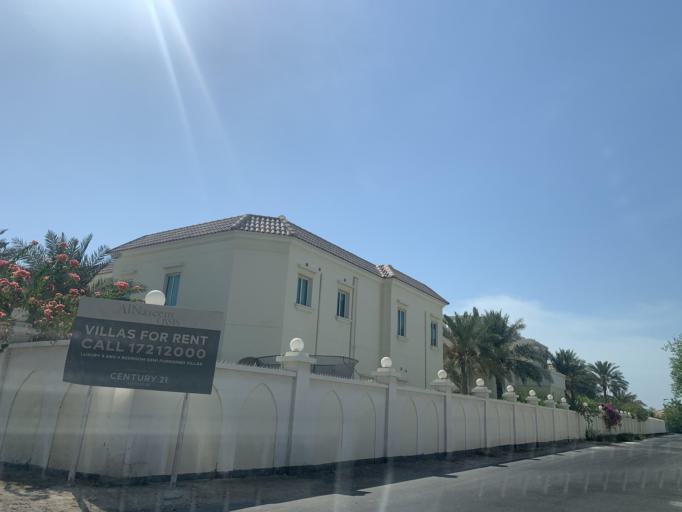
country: BH
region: Northern
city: Madinat `Isa
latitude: 26.1923
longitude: 50.4733
